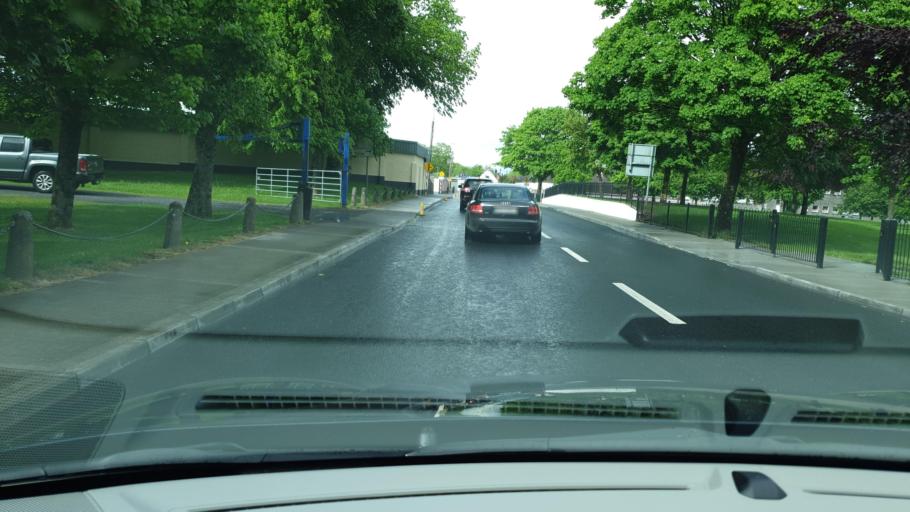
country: IE
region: Connaught
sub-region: County Galway
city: Ballinasloe
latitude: 53.3295
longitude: -8.2286
